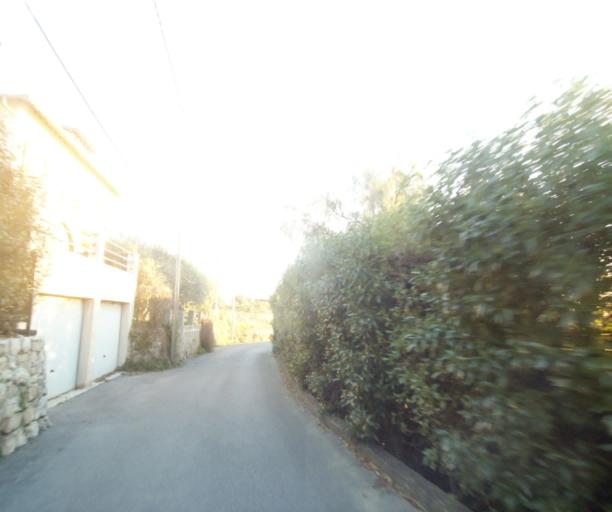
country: FR
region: Provence-Alpes-Cote d'Azur
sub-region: Departement des Alpes-Maritimes
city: Vallauris
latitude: 43.5878
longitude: 7.0724
